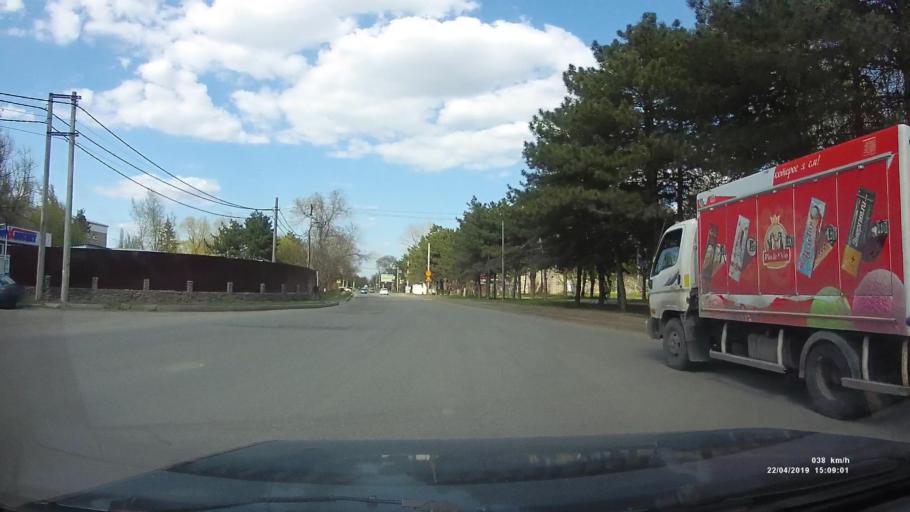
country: RU
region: Rostov
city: Azov
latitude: 47.0984
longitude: 39.4101
